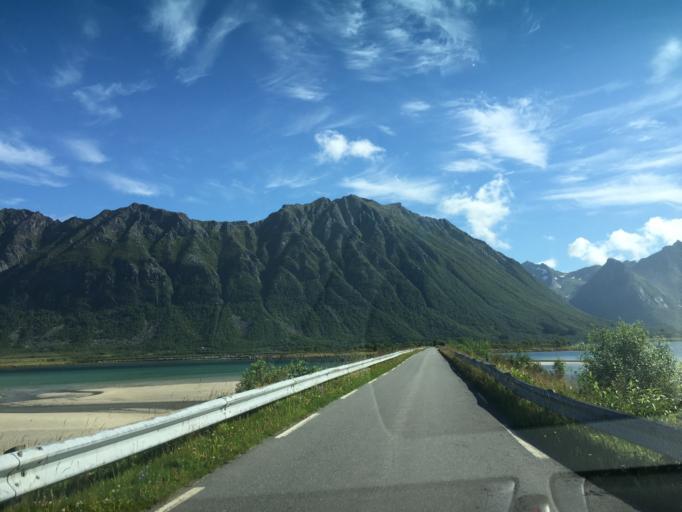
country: NO
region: Nordland
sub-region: Vagan
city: Svolvaer
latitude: 68.3951
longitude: 14.5469
